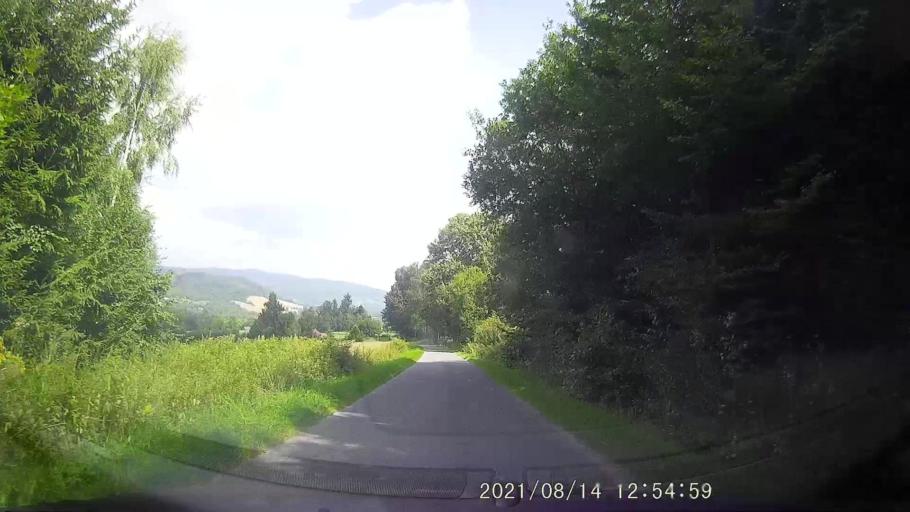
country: PL
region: Lower Silesian Voivodeship
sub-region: Powiat klodzki
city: Ladek-Zdroj
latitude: 50.3299
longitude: 16.8252
